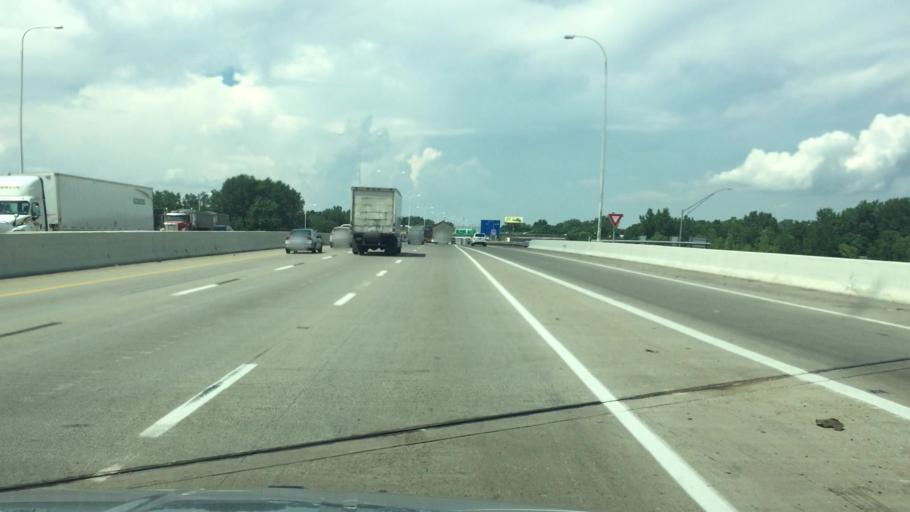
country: US
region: Ohio
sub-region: Lucas County
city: Toledo
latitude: 41.6748
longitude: -83.5151
